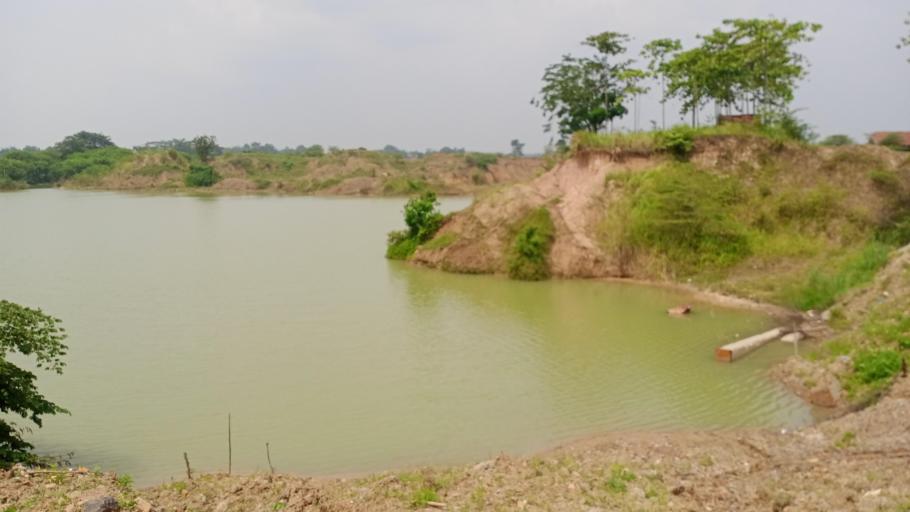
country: ID
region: West Java
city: Cileungsir
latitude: -6.4208
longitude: 107.1050
